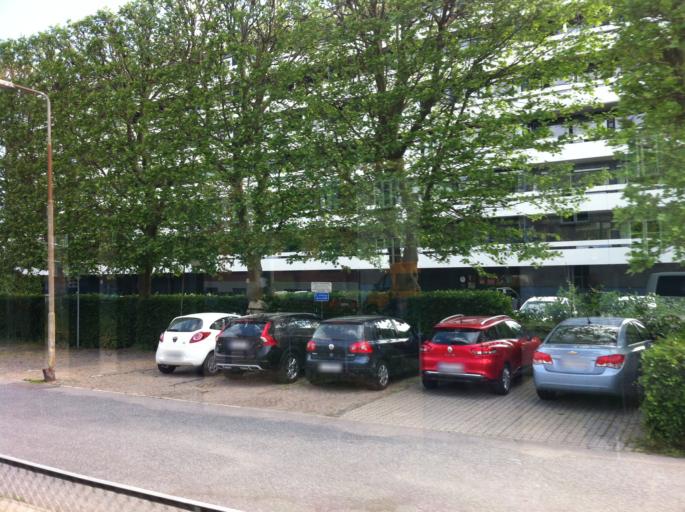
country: DK
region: Capital Region
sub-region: Helsingor Kommune
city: Helsingor
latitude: 56.0399
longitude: 12.6118
